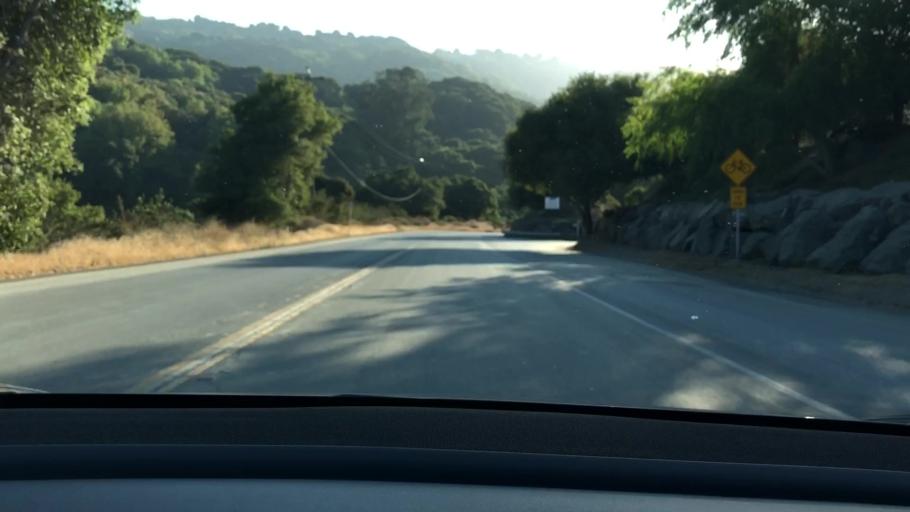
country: US
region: California
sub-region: Santa Clara County
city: Cupertino
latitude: 37.2961
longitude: -122.0812
